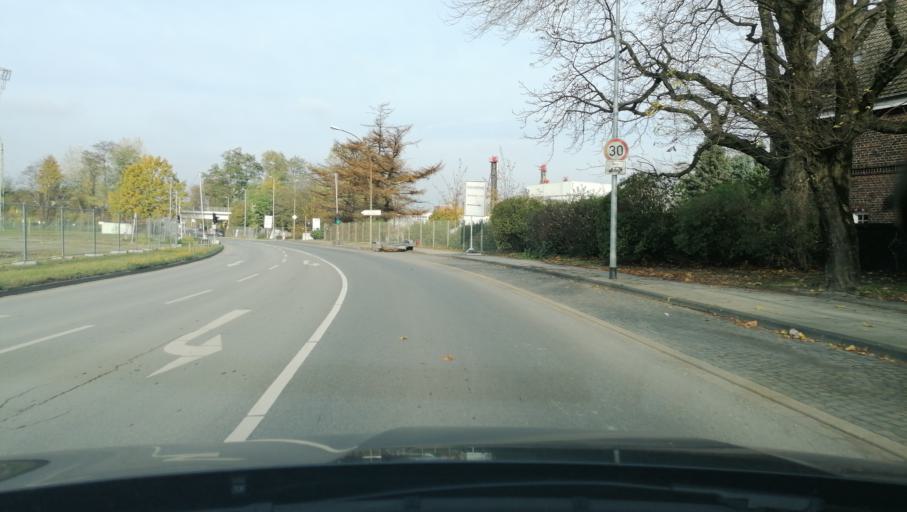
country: DE
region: North Rhine-Westphalia
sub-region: Regierungsbezirk Arnsberg
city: Herne
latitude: 51.5468
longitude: 7.1813
